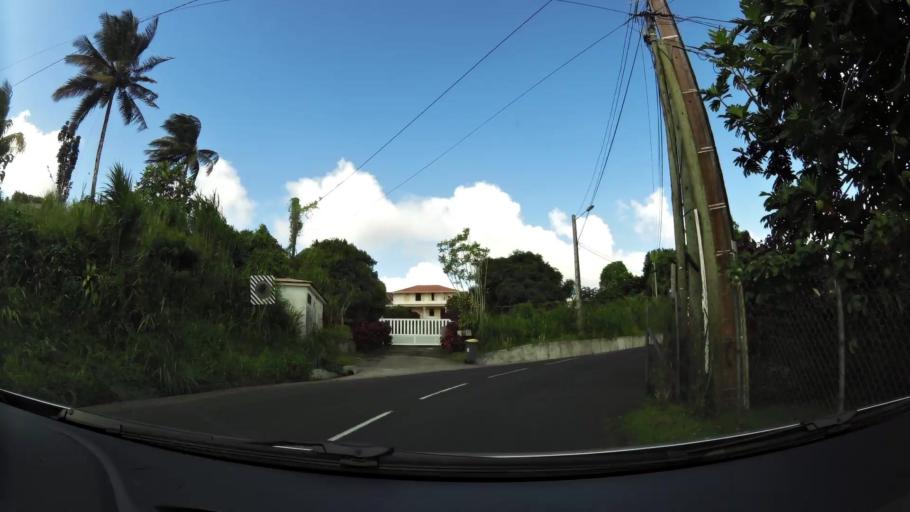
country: MQ
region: Martinique
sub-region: Martinique
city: Fort-de-France
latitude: 14.6538
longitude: -61.0857
